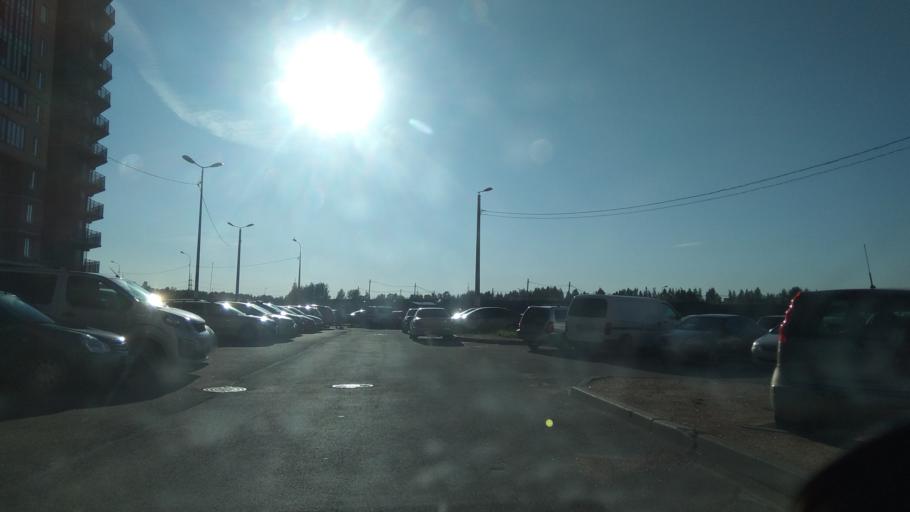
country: RU
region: Leningrad
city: Parnas
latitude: 60.0822
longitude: 30.3404
